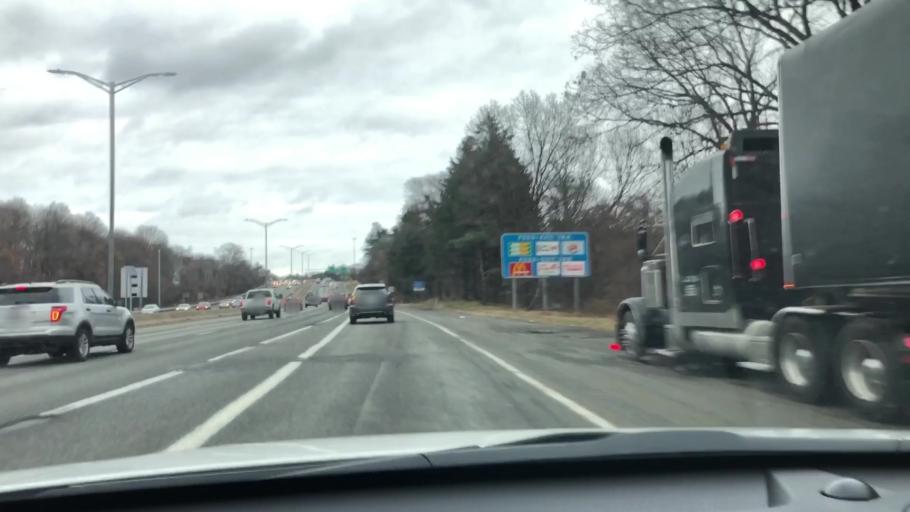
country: US
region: Massachusetts
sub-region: Middlesex County
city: Stoneham
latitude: 42.5016
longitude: -71.1125
